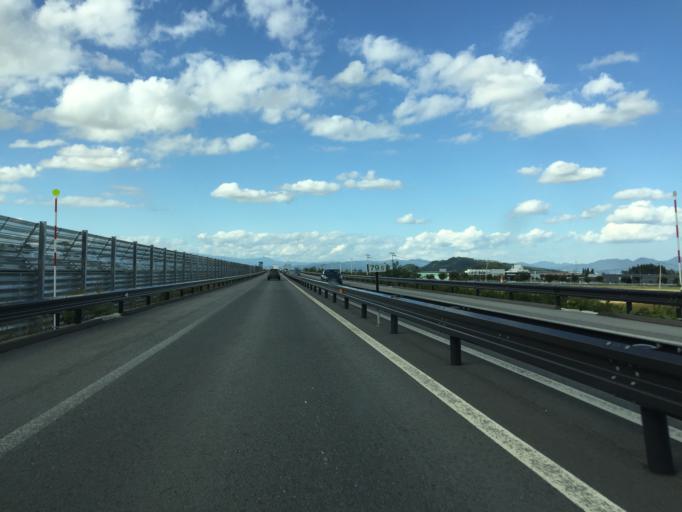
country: JP
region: Yamagata
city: Yonezawa
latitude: 37.9050
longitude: 140.1432
